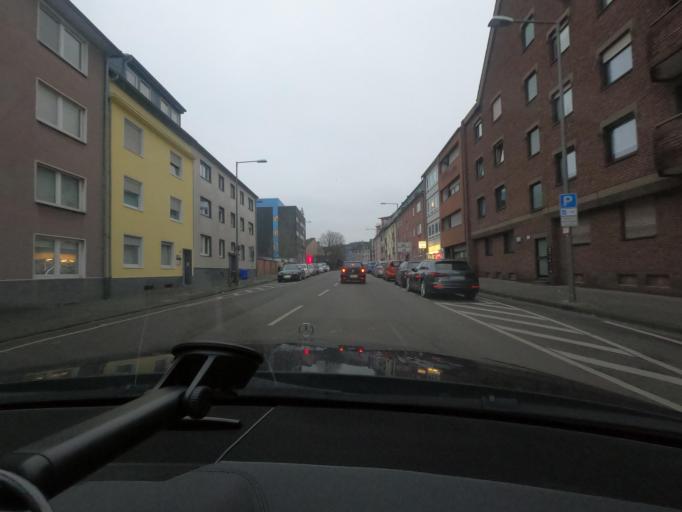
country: DE
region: North Rhine-Westphalia
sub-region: Regierungsbezirk Dusseldorf
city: Krefeld
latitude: 51.3384
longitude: 6.5654
